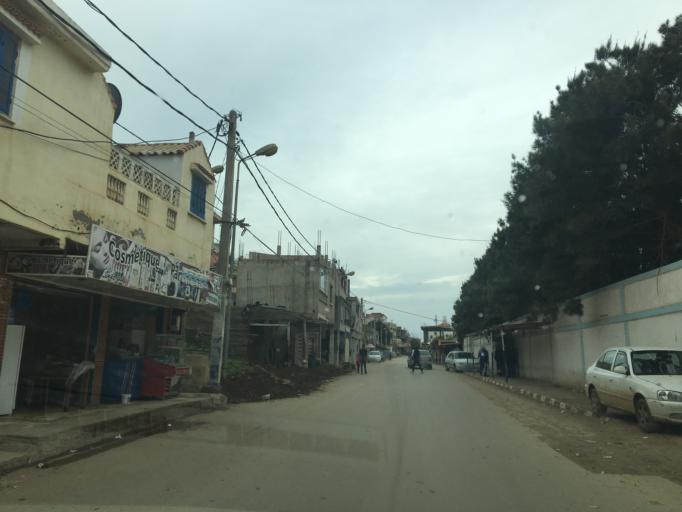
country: DZ
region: Tipaza
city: Tipasa
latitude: 36.6416
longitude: 2.3590
